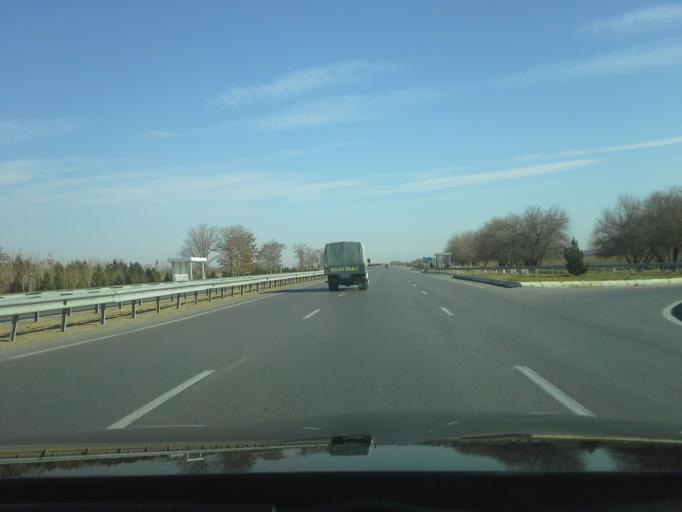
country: TM
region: Ahal
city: Annau
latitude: 37.9035
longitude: 58.5517
